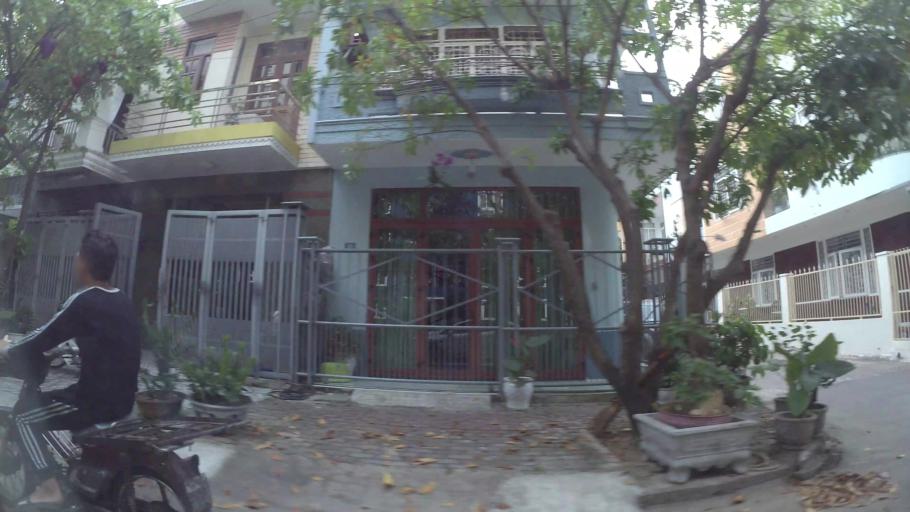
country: VN
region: Da Nang
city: Son Tra
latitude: 16.0566
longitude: 108.2350
